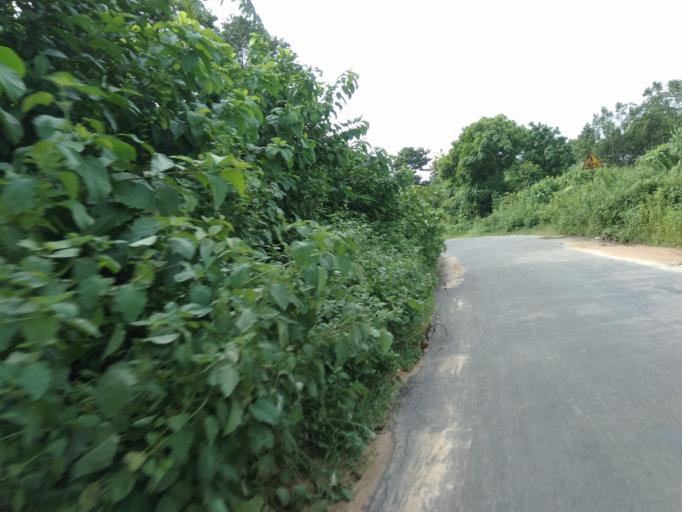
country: BD
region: Chittagong
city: Khagrachhari
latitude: 23.0380
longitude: 92.0042
